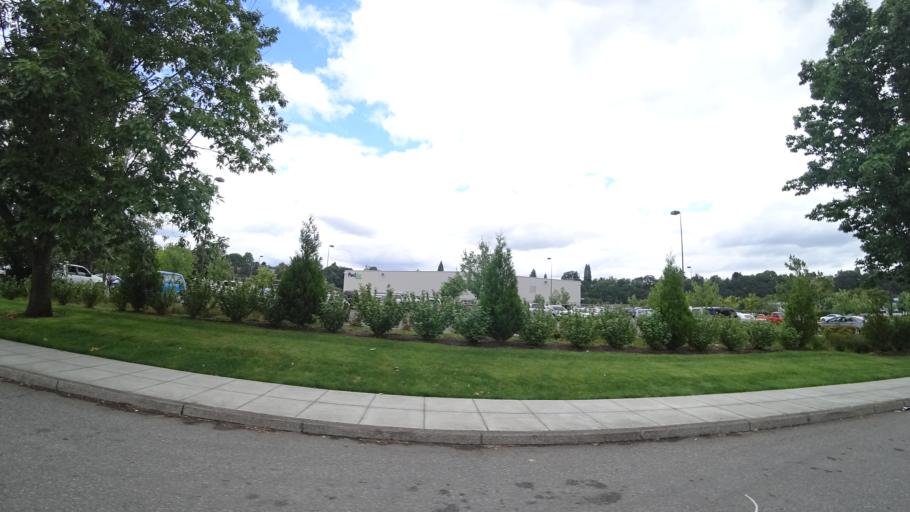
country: US
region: Oregon
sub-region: Multnomah County
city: Portland
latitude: 45.5698
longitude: -122.7074
